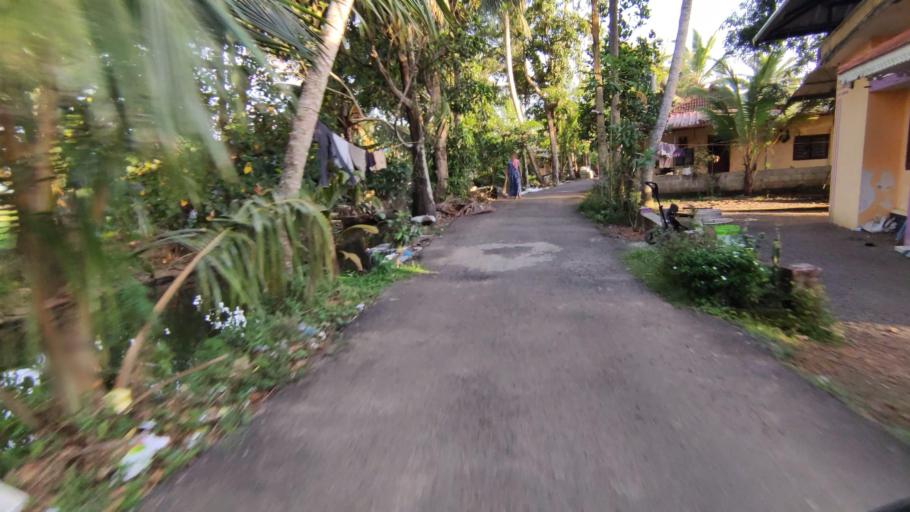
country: IN
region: Kerala
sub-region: Kottayam
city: Kottayam
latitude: 9.5778
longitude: 76.4541
